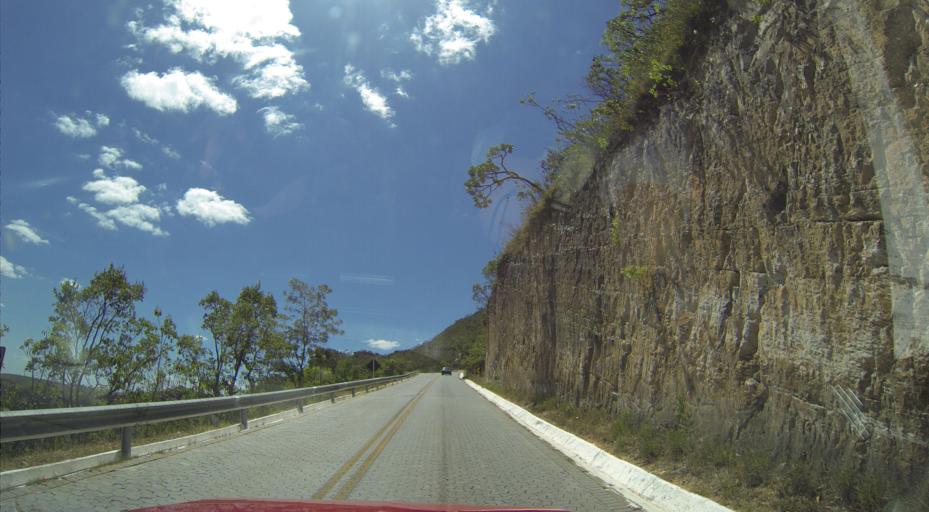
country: BR
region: Minas Gerais
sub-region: Conceicao Do Mato Dentro
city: Conceicao do Mato Dentro
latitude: -19.3090
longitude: -43.6042
